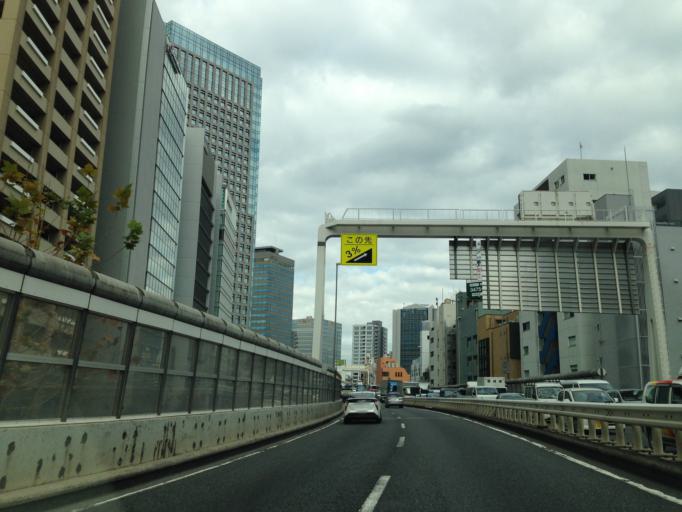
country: JP
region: Tokyo
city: Tokyo
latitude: 35.6986
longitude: 139.7522
